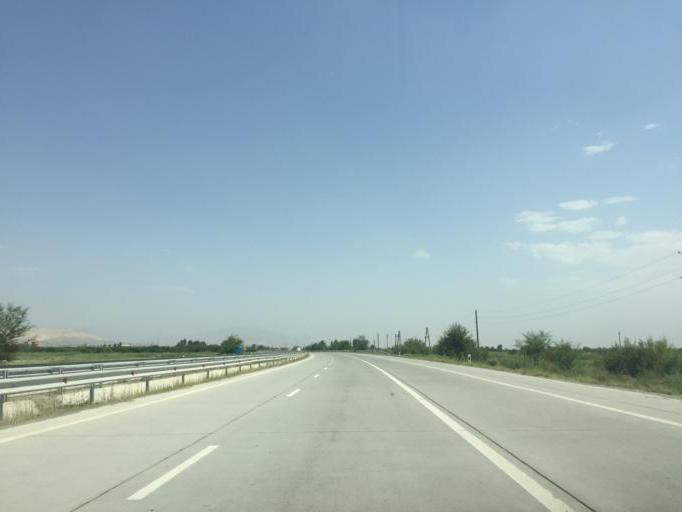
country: AM
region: Ararat
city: Berkanush
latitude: 39.9612
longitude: 44.5161
